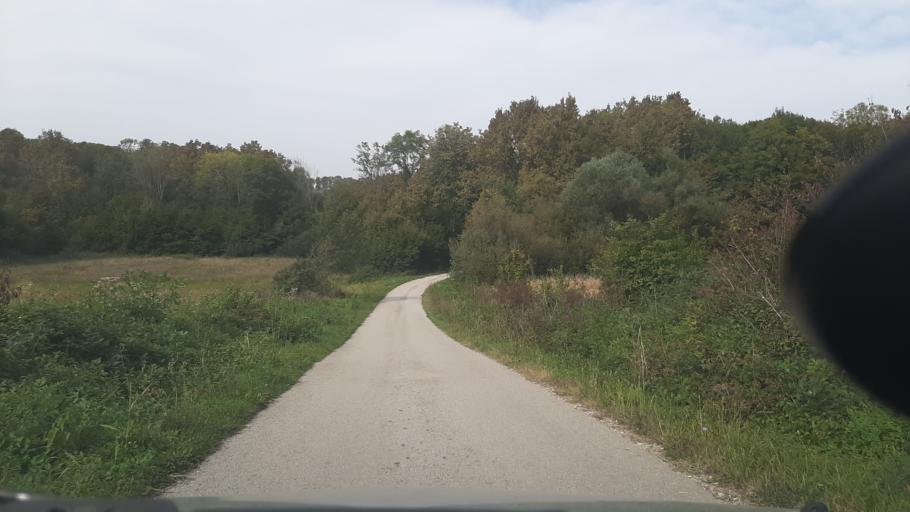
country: BA
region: Republika Srpska
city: Maglajani
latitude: 44.8694
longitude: 17.4704
